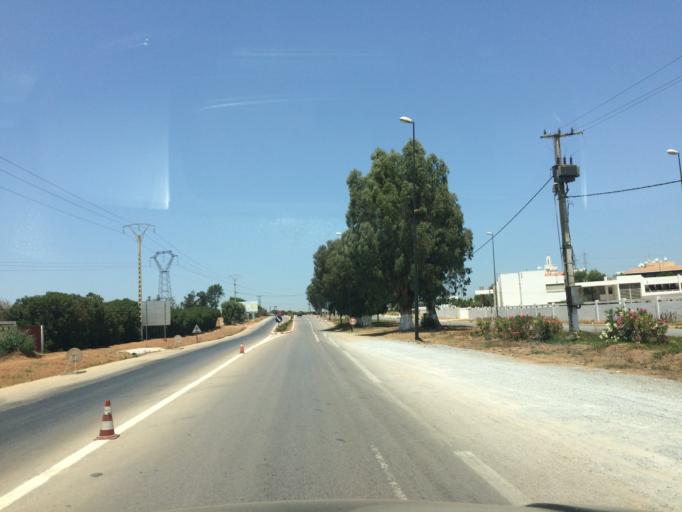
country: MA
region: Rabat-Sale-Zemmour-Zaer
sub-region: Skhirate-Temara
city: Temara
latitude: 33.8525
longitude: -6.8538
